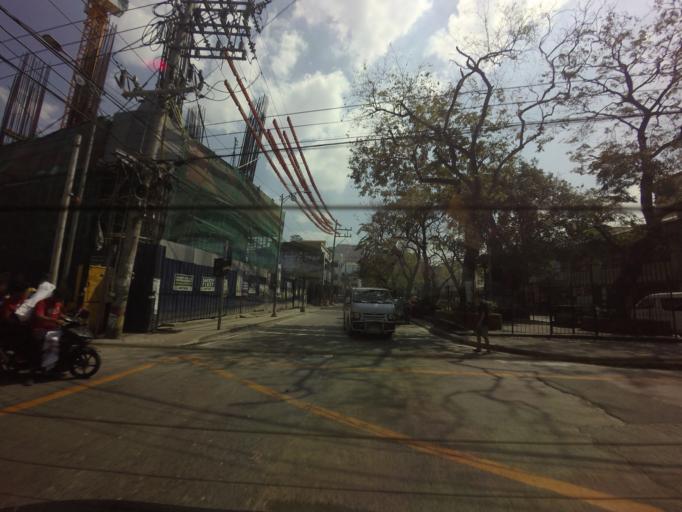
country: PH
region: Metro Manila
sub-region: City of Manila
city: Manila
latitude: 14.6099
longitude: 120.9679
